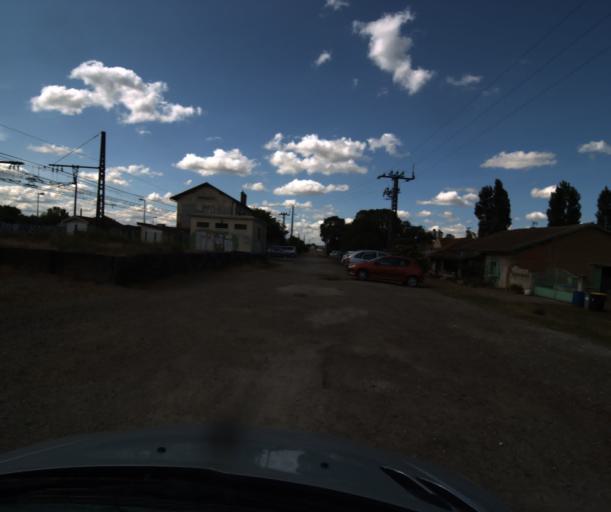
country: FR
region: Midi-Pyrenees
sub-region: Departement du Tarn-et-Garonne
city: Finhan
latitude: 43.9247
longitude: 1.2644
